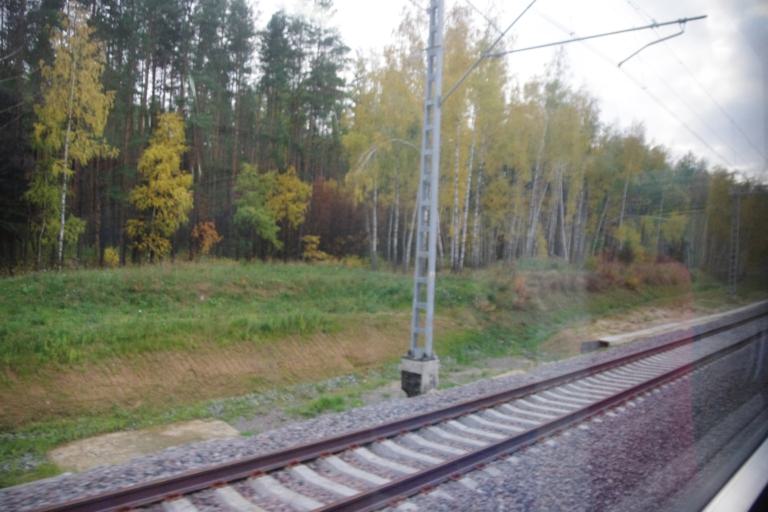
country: RU
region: Moskovskaya
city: Vostryakovo
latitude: 55.4367
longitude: 37.8654
